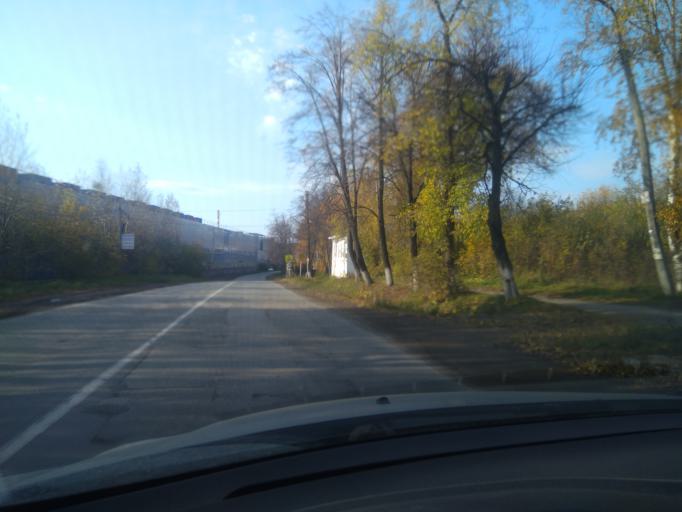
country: RU
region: Sverdlovsk
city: Nizhniye Sergi
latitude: 56.6672
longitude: 59.3155
